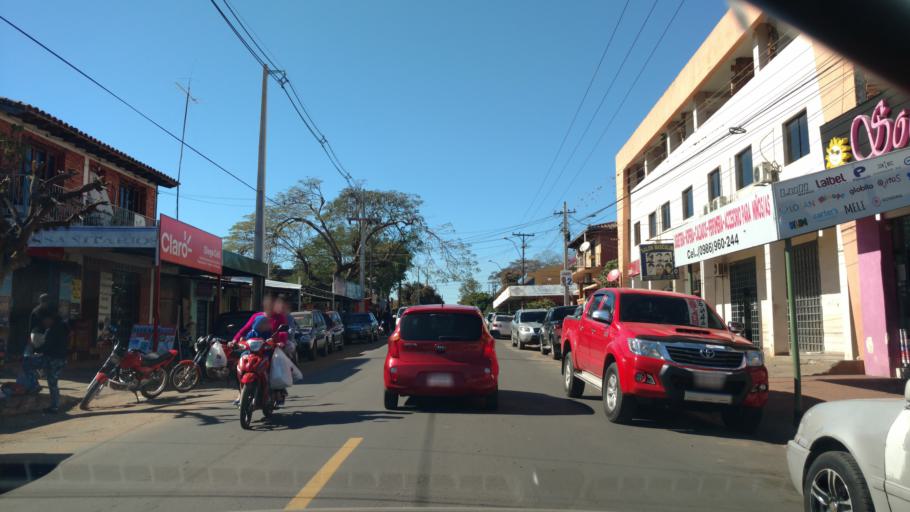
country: PY
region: Central
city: Itaugua
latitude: -25.3962
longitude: -57.3491
